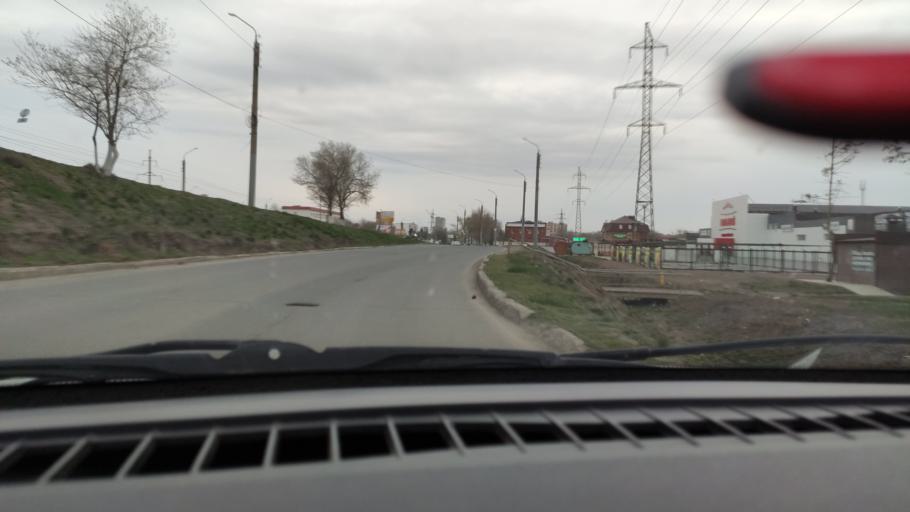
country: RU
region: Orenburg
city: Orenburg
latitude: 51.8284
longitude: 55.1079
